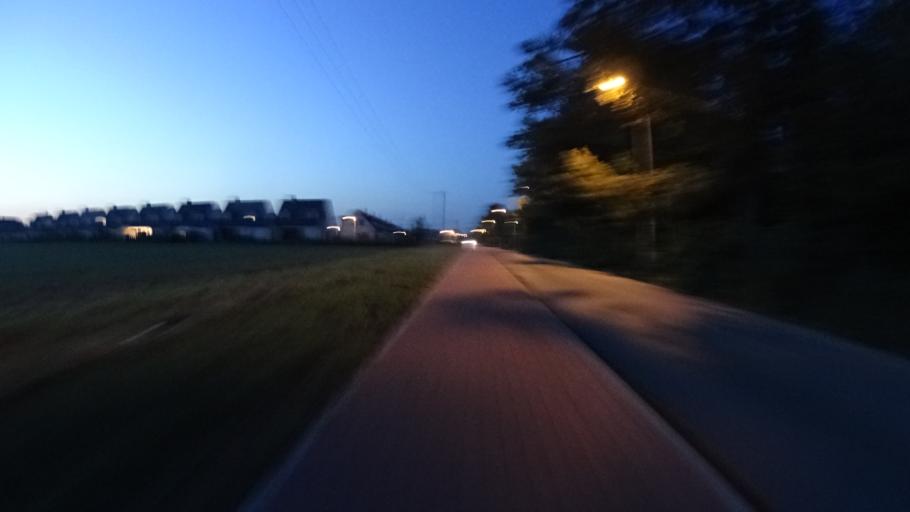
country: PL
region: Masovian Voivodeship
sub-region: Powiat warszawski zachodni
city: Ozarow Mazowiecki
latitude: 52.2329
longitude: 20.7803
